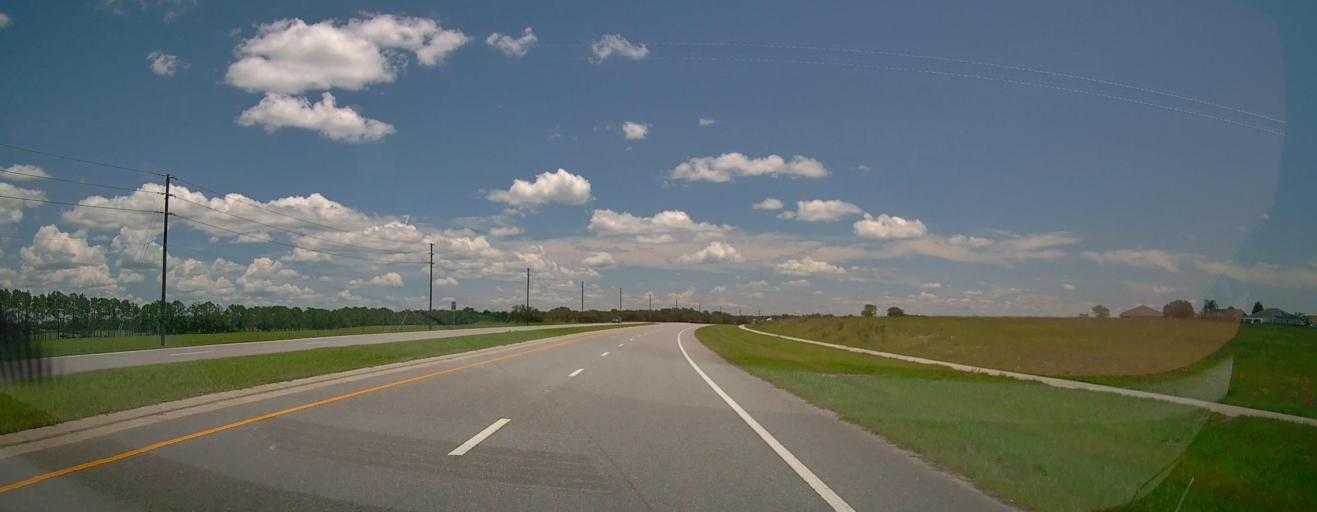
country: US
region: Florida
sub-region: Marion County
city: Silver Springs Shores
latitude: 29.0860
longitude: -82.0486
